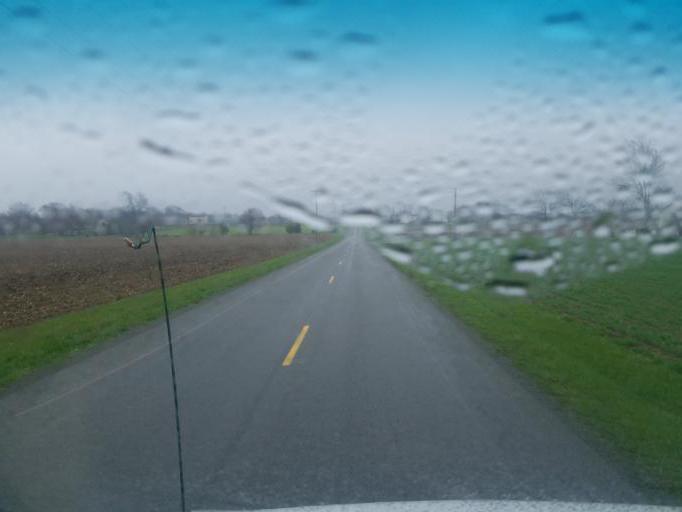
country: US
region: Ohio
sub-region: Wyandot County
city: Carey
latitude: 40.9922
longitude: -83.3895
